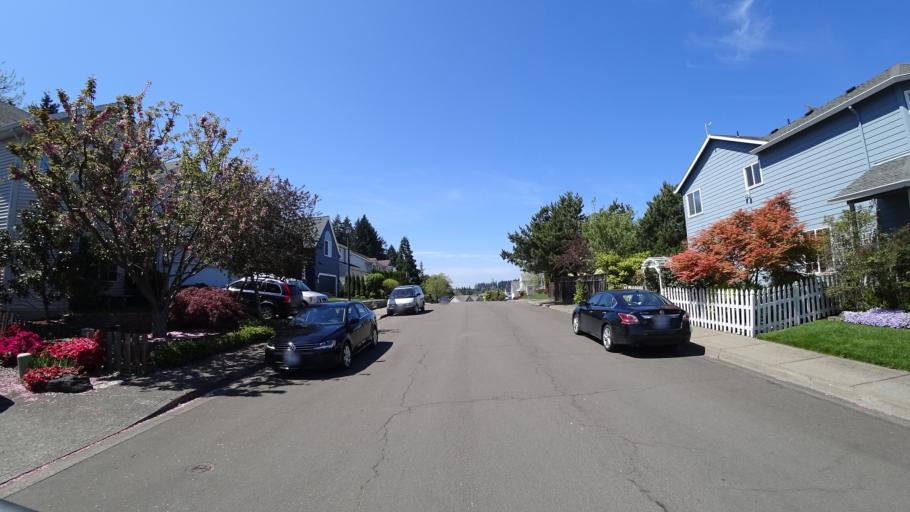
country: US
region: Oregon
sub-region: Washington County
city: King City
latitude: 45.4298
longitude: -122.8176
